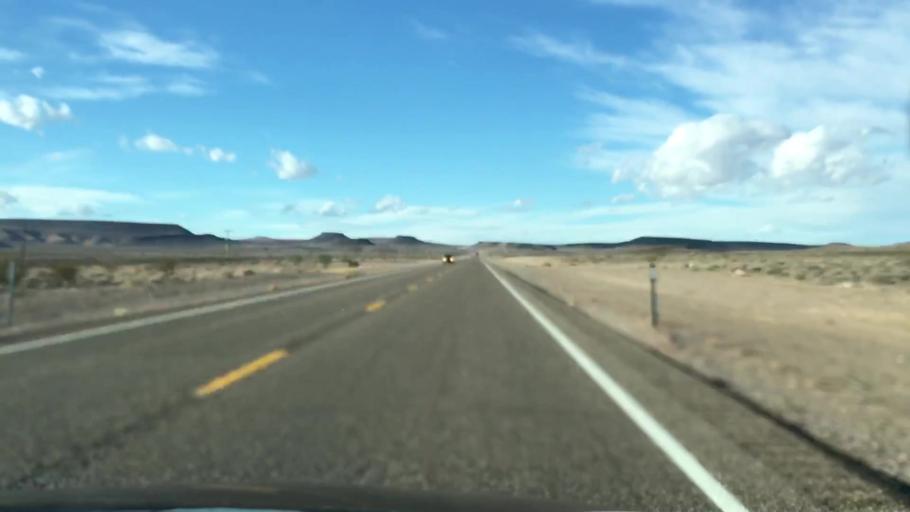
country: US
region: Nevada
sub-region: Esmeralda County
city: Goldfield
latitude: 37.3554
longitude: -117.1108
